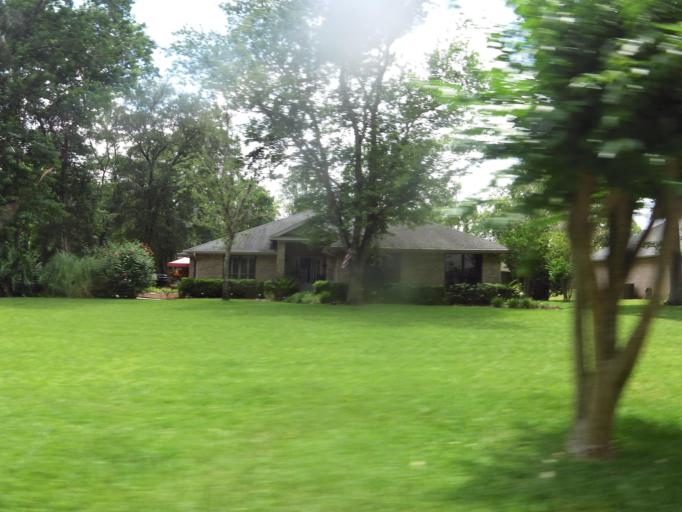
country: US
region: Florida
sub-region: Clay County
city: Orange Park
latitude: 30.1892
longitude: -81.6973
